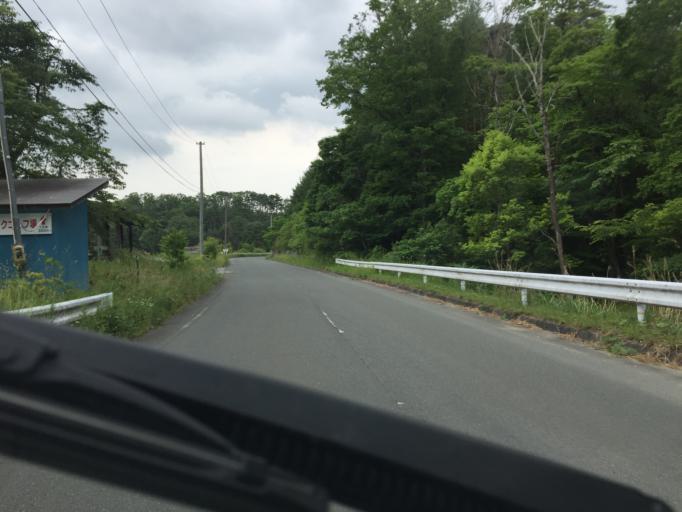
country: JP
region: Miyagi
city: Marumori
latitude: 37.8593
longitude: 140.8738
